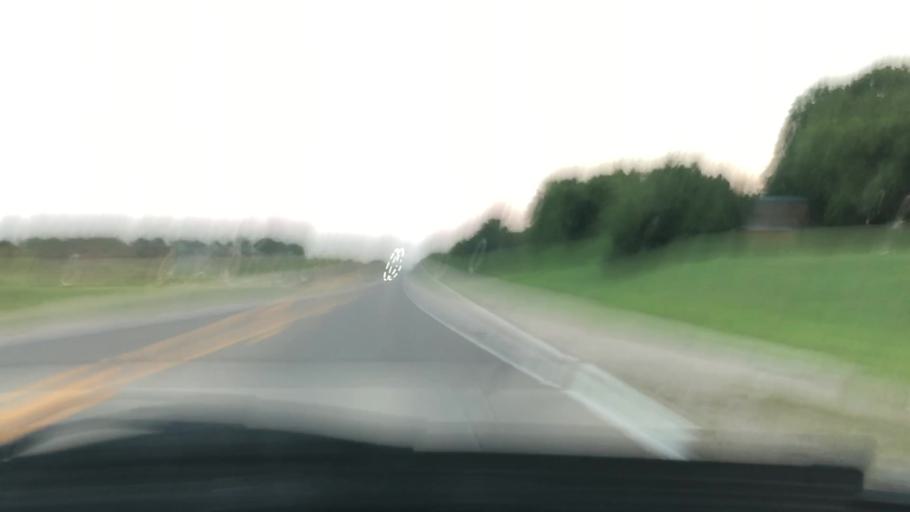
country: US
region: Iowa
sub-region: Henry County
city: Mount Pleasant
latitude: 40.9628
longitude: -91.5394
